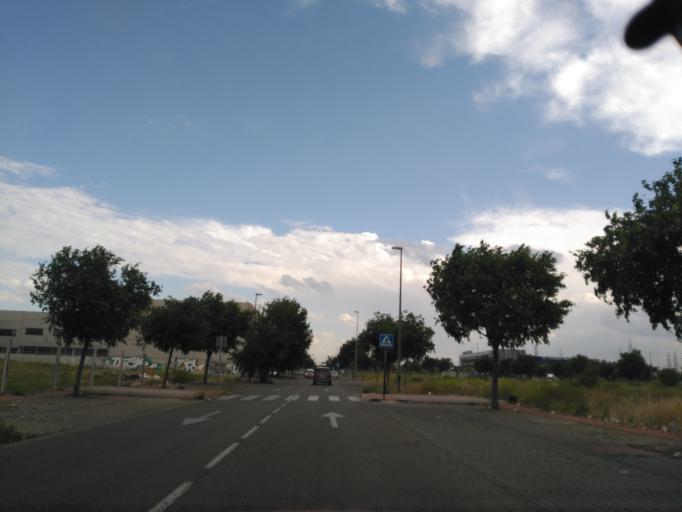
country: ES
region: Madrid
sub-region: Provincia de Madrid
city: Villaverde
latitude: 40.3390
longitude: -3.7178
